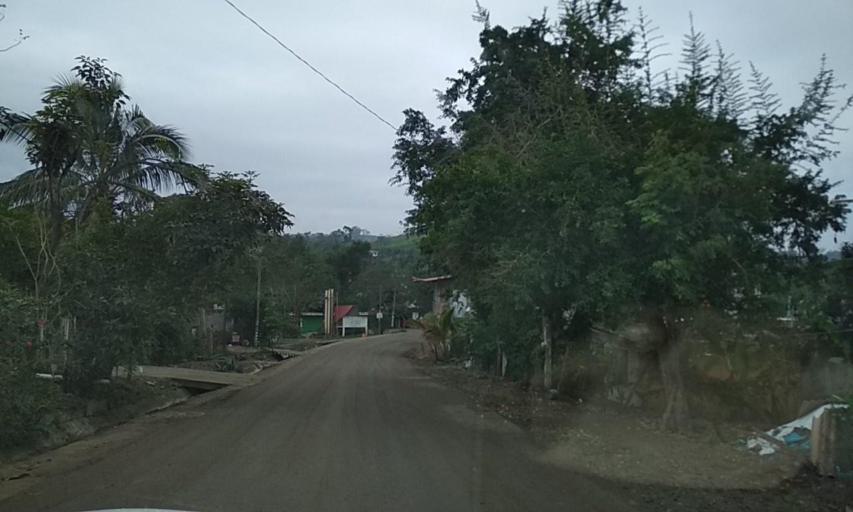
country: MX
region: Veracruz
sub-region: Coatzintla
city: Manuel Maria Contreras
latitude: 20.4491
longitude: -97.4805
